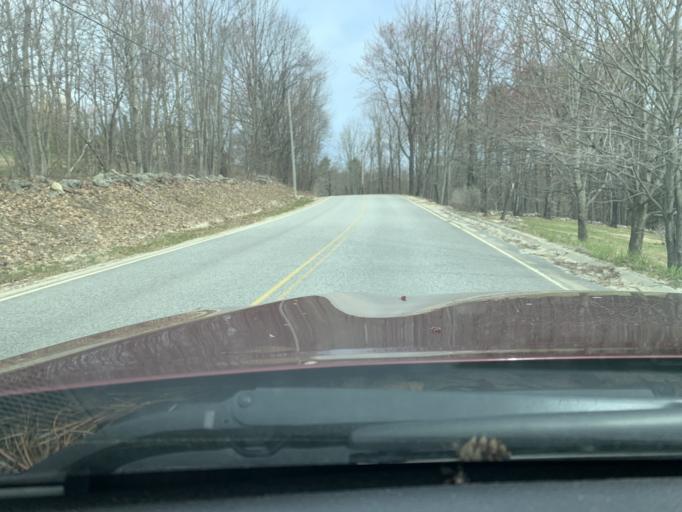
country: US
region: Maine
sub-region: Cumberland County
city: Raymond
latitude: 43.9525
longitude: -70.3864
